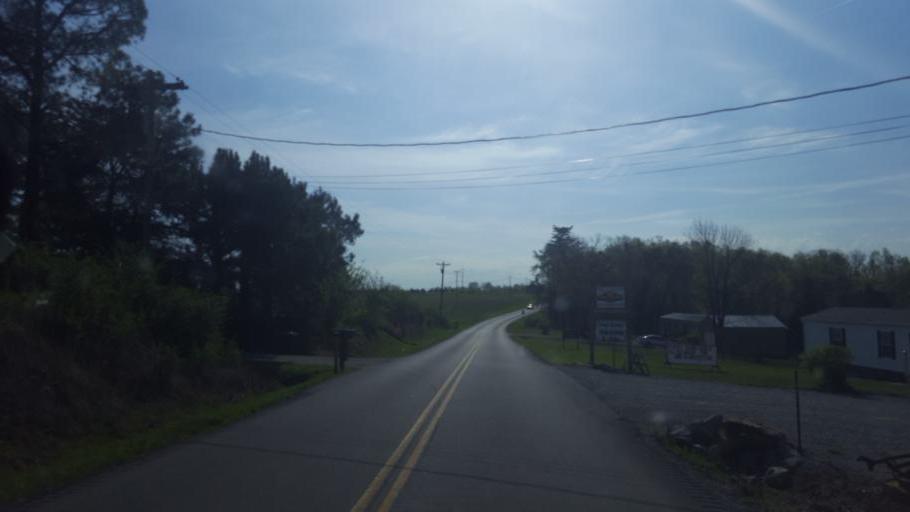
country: US
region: Kentucky
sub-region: Edmonson County
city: Brownsville
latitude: 37.2703
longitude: -86.1642
